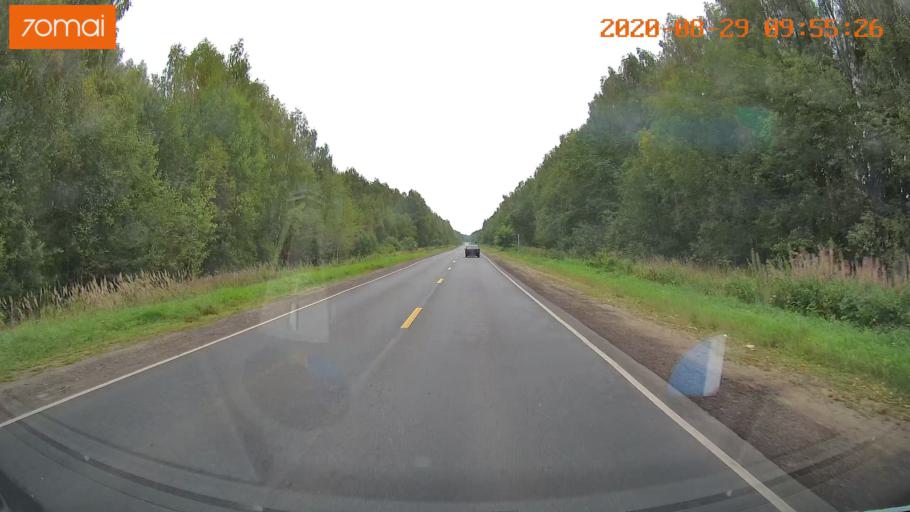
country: RU
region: Ivanovo
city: Zarechnyy
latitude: 57.4223
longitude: 42.2634
